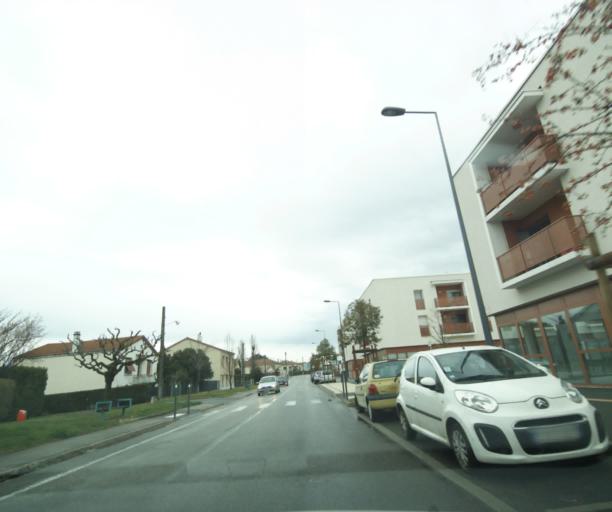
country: FR
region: Rhone-Alpes
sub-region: Departement de la Drome
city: Valence
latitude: 44.9505
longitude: 4.8879
